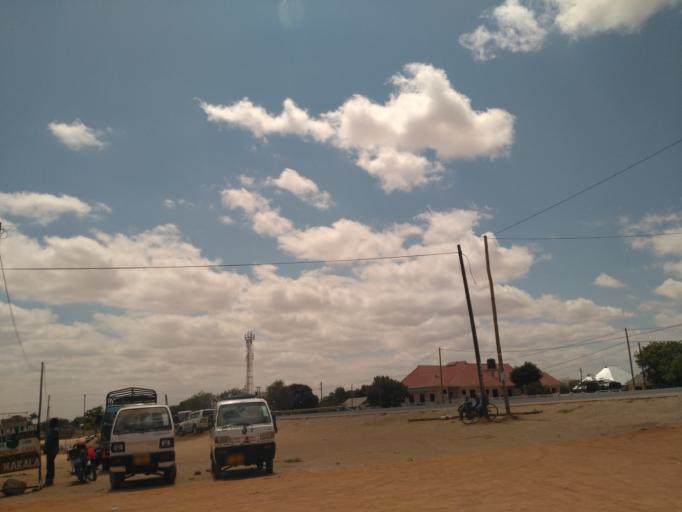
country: TZ
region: Dodoma
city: Kisasa
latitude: -6.1661
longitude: 35.7840
